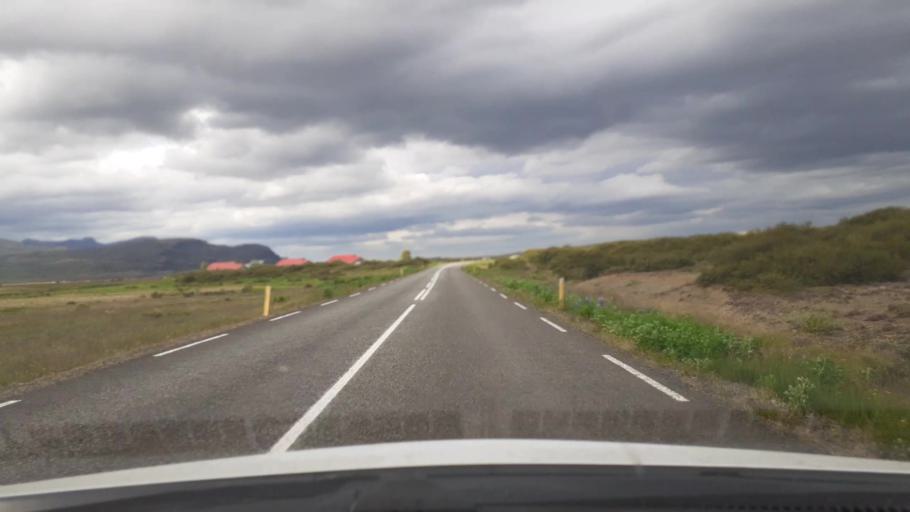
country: IS
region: West
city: Borgarnes
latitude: 64.5432
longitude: -21.6233
